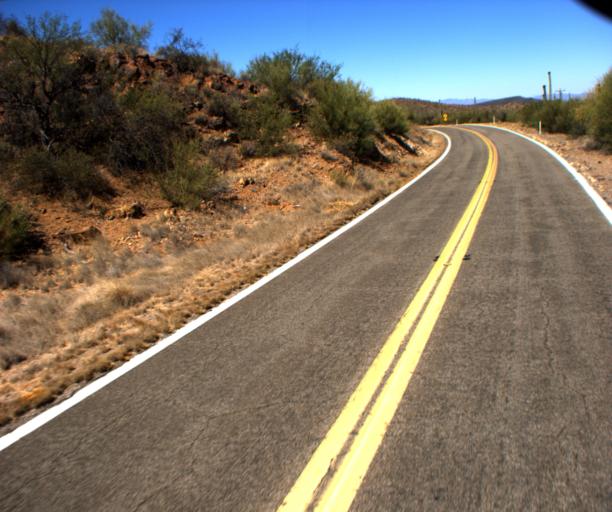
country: US
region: Arizona
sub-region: Pima County
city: Sells
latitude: 32.1750
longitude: -112.1983
